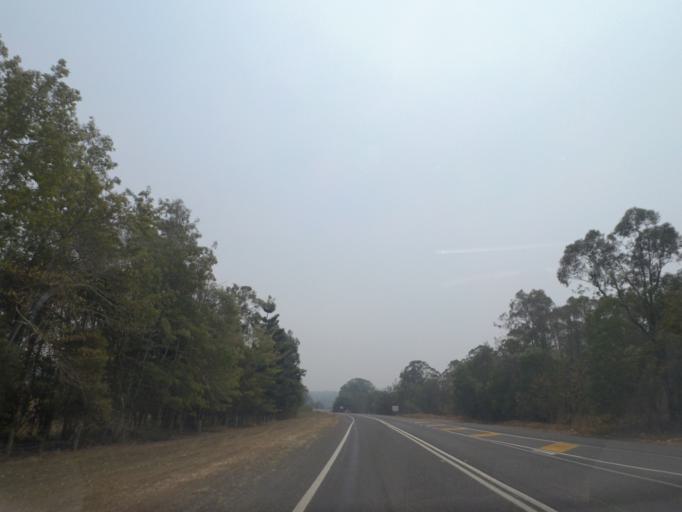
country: AU
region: New South Wales
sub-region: Clarence Valley
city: Maclean
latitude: -29.5483
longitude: 153.1561
